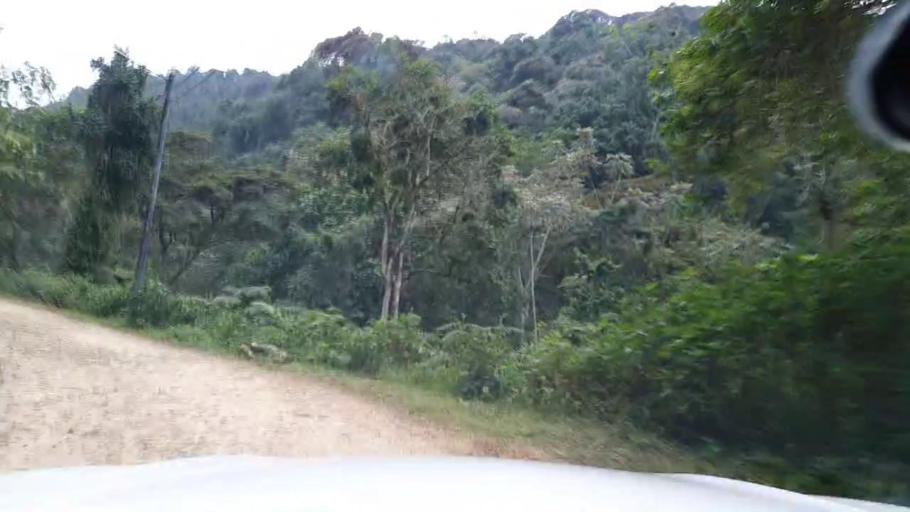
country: RW
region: Western Province
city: Cyangugu
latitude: -2.5703
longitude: 29.2266
